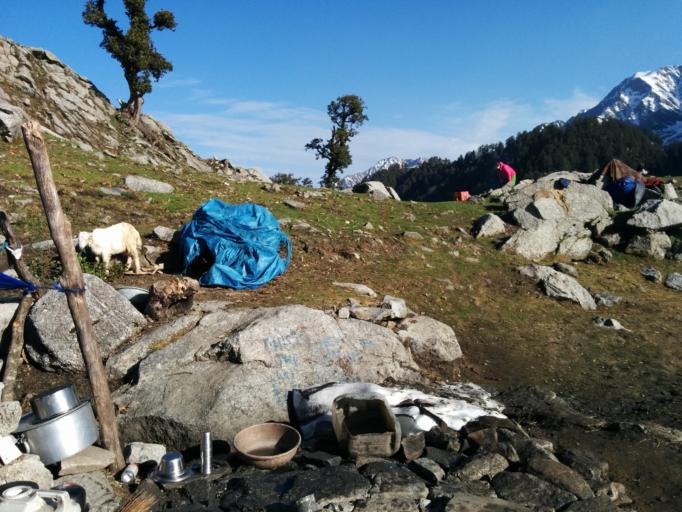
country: IN
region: Himachal Pradesh
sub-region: Kangra
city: Dharmsala
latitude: 32.2740
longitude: 76.3616
